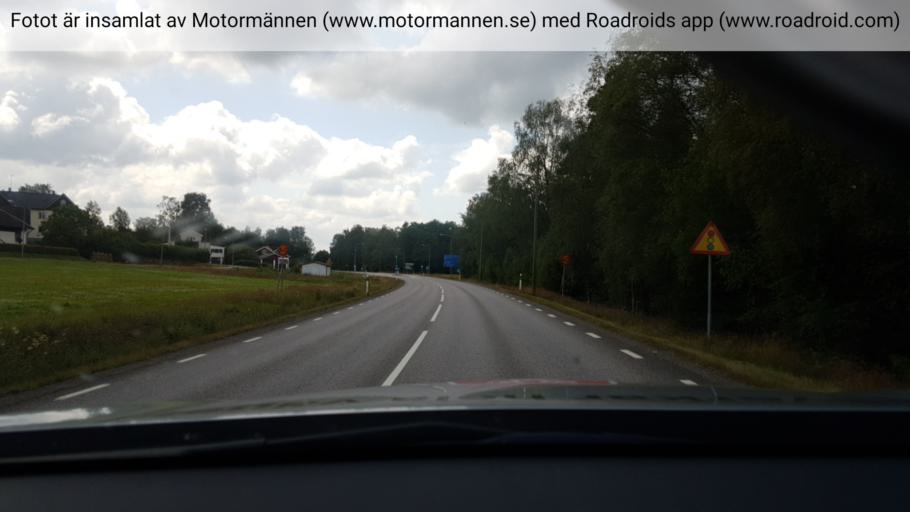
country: SE
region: Vaestra Goetaland
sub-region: Svenljunga Kommun
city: Svenljunga
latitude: 57.4154
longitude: 12.9749
